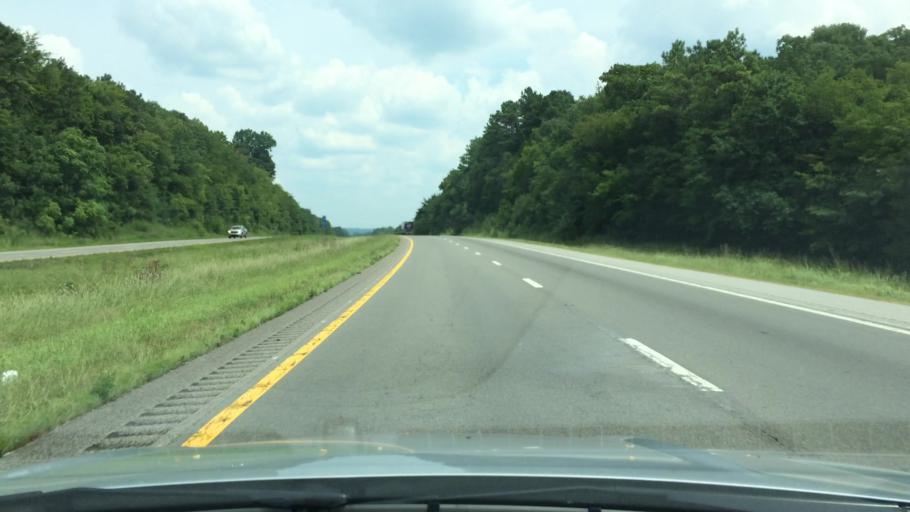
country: US
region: Tennessee
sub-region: Marshall County
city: Cornersville
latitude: 35.2797
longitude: -86.8864
